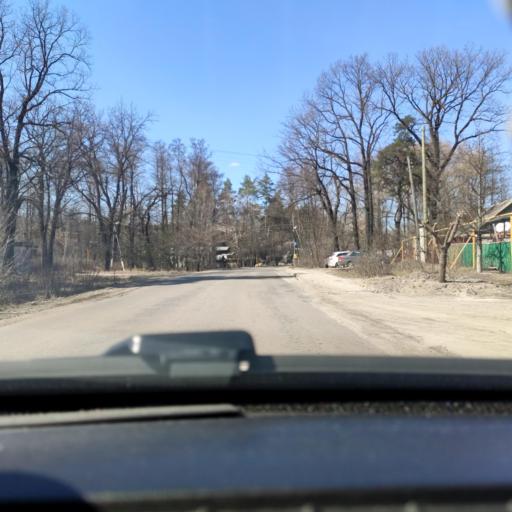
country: RU
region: Voronezj
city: Somovo
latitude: 51.7299
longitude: 39.3643
